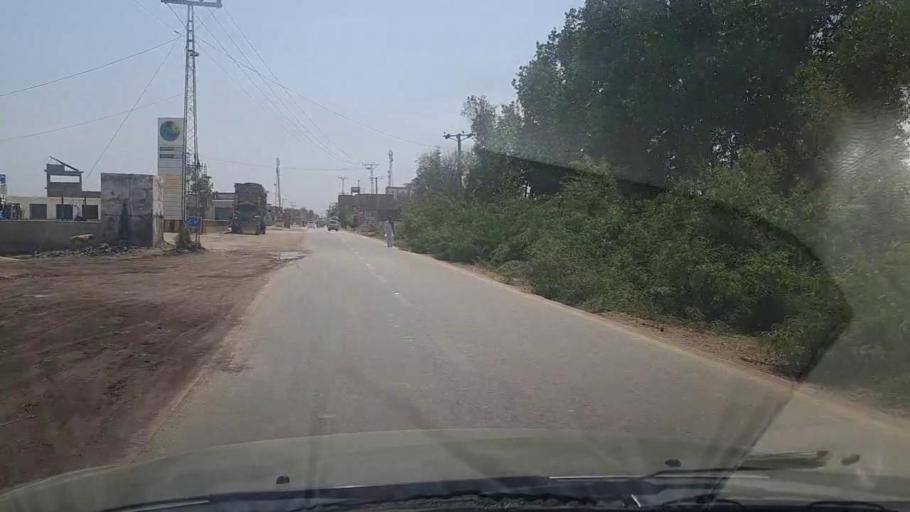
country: PK
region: Sindh
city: Hyderabad
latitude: 25.3880
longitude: 68.4237
